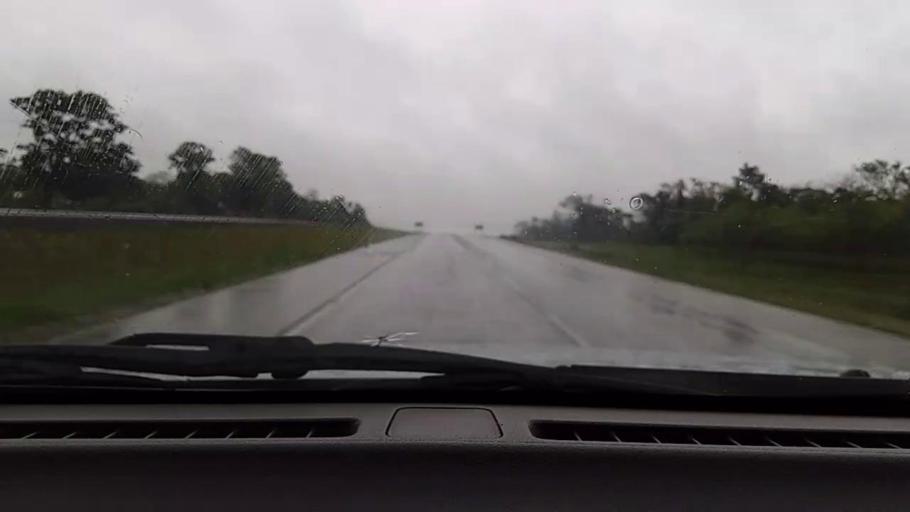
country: PY
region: Caaguazu
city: Repatriacion
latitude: -25.4661
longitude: -55.9452
